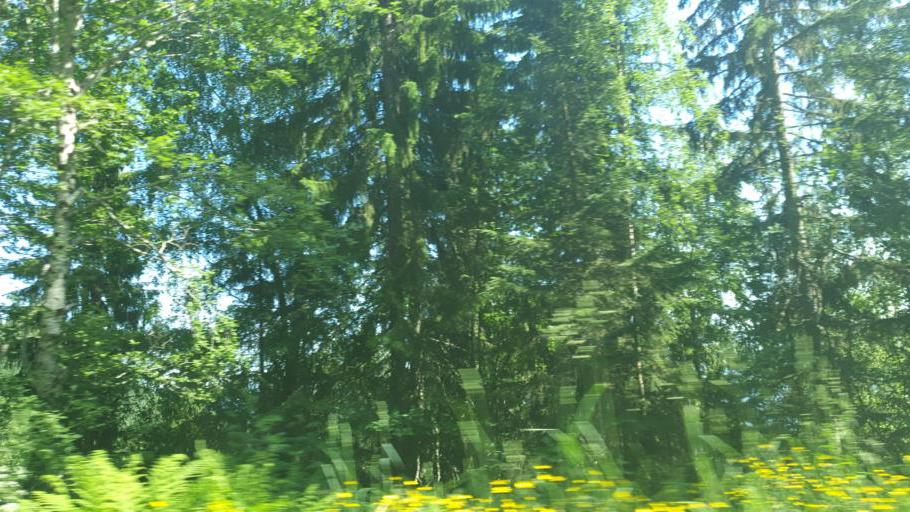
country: NO
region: Nord-Trondelag
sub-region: Frosta
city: Frosta
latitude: 63.7085
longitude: 10.7708
